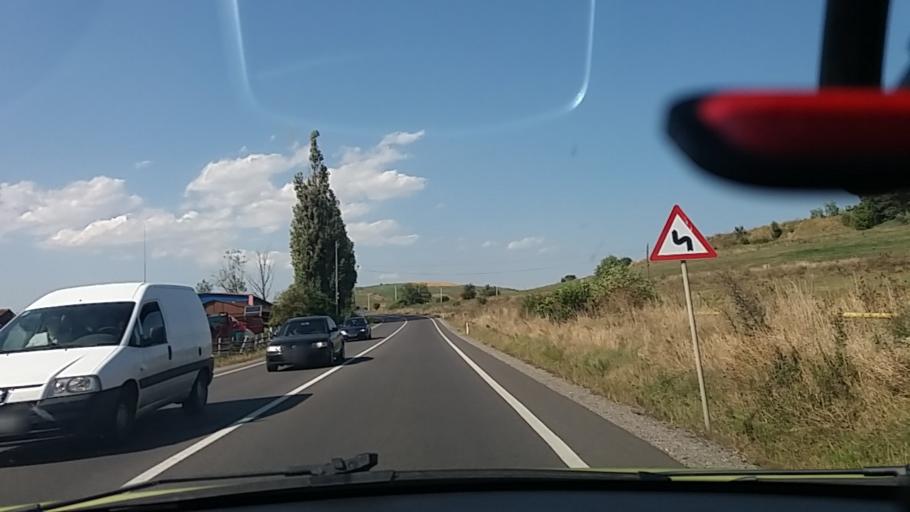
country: RO
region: Sibiu
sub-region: Comuna Sura Mare
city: Sura Mare
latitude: 45.8392
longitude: 24.1508
